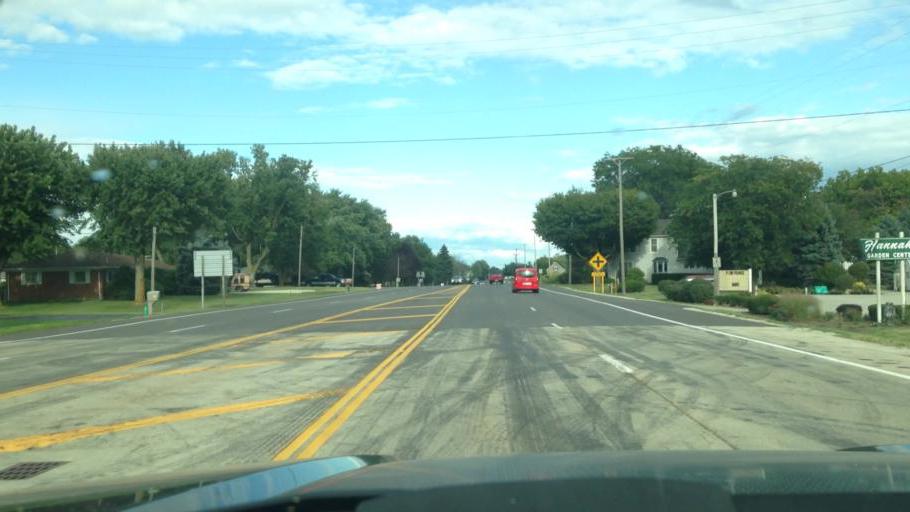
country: US
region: Ohio
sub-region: Darke County
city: Greenville
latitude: 40.0998
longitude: -84.6031
